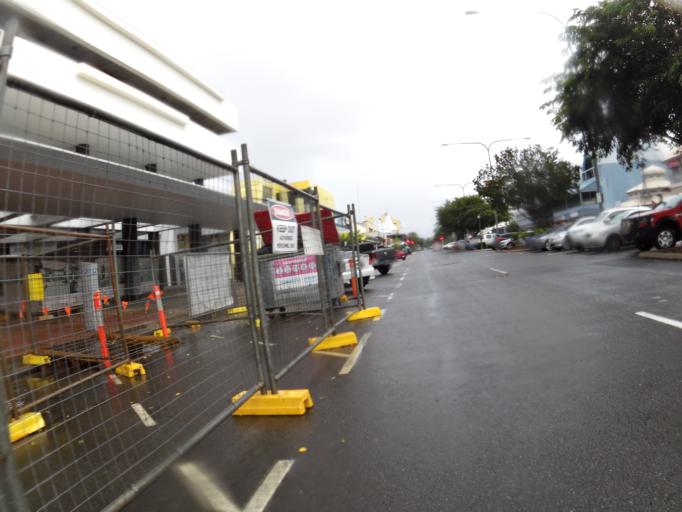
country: AU
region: Queensland
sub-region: Cairns
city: Cairns
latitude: -16.9250
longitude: 145.7782
